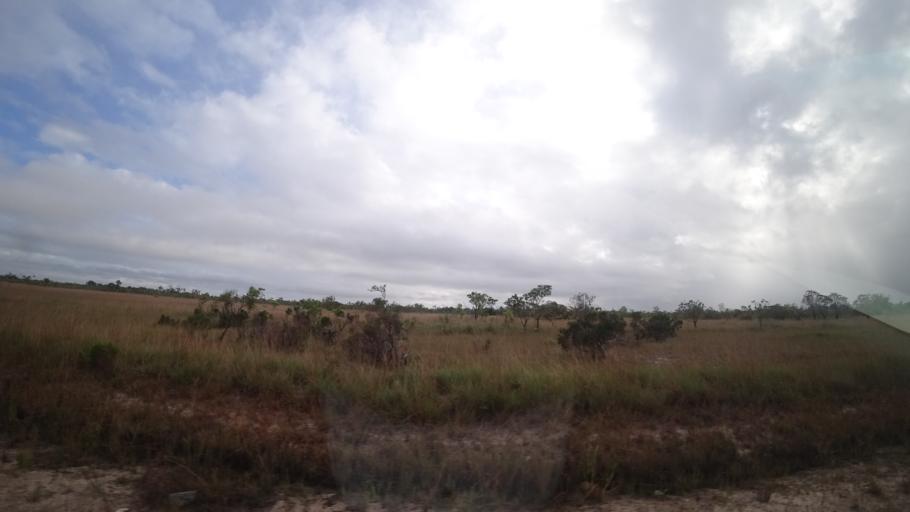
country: MZ
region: Sofala
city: Beira
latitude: -19.6127
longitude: 35.0739
